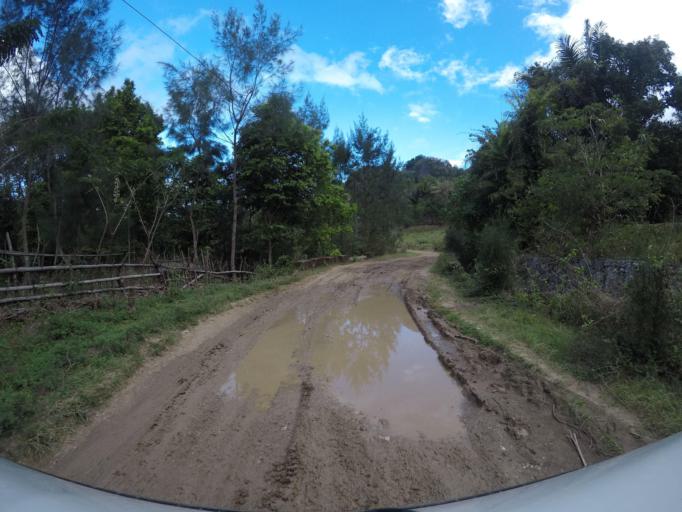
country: TL
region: Baucau
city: Venilale
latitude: -8.6837
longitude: 126.6523
